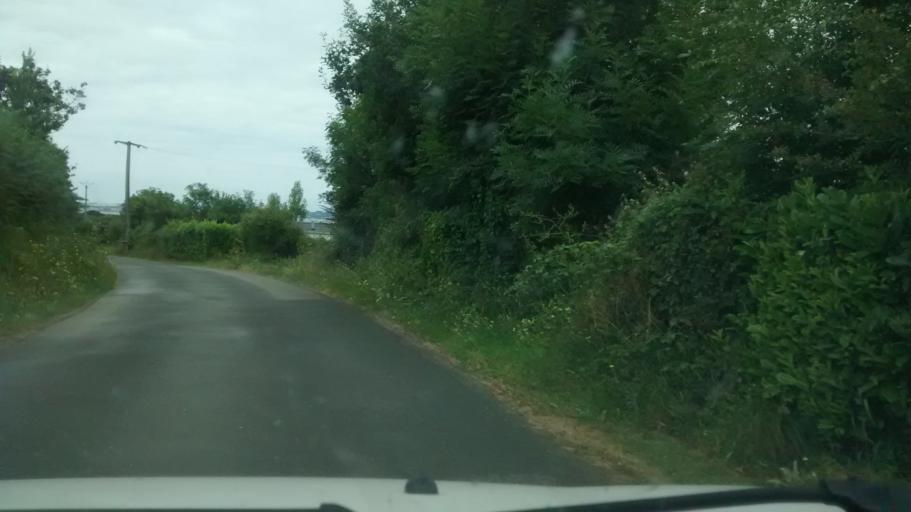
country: FR
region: Brittany
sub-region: Departement du Finistere
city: Lanveoc
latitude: 48.3293
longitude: -4.4445
